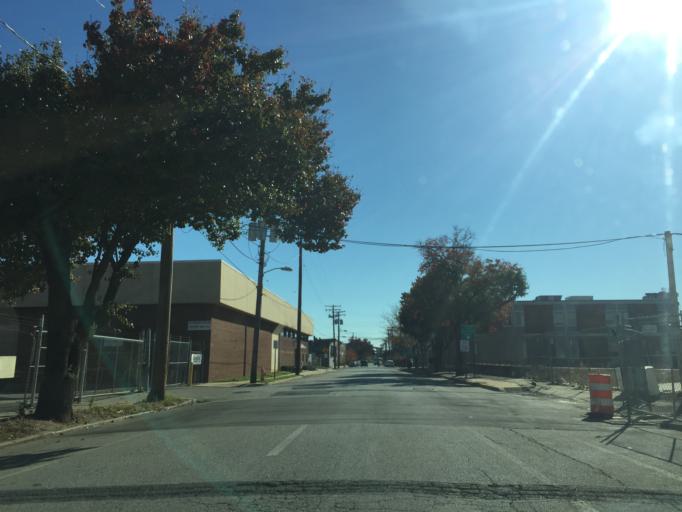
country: US
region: Maryland
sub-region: City of Baltimore
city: Baltimore
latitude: 39.2770
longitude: -76.6362
